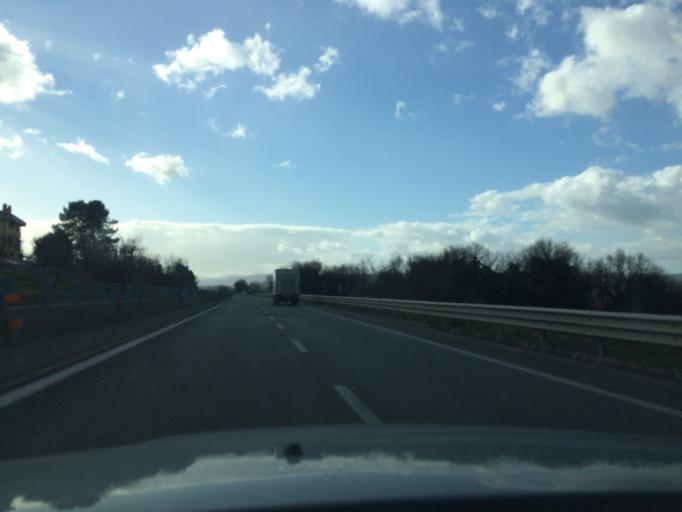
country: IT
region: Umbria
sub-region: Provincia di Perugia
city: Collepepe
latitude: 42.9035
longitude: 12.3904
